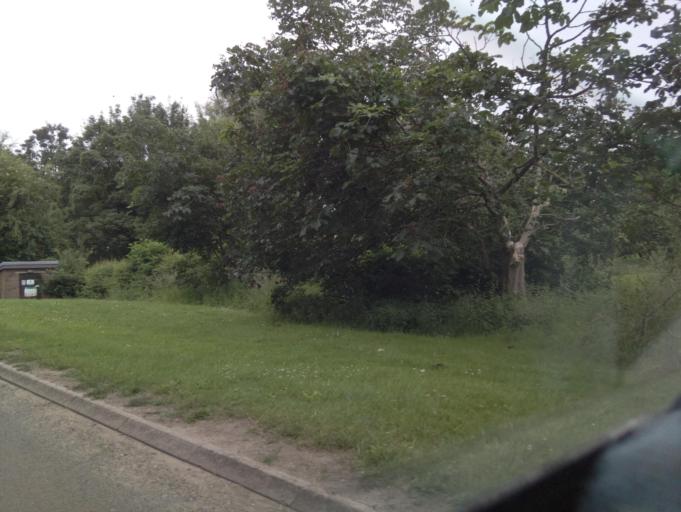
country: GB
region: England
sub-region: District of Rutland
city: Empingham
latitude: 52.6640
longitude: -0.5955
